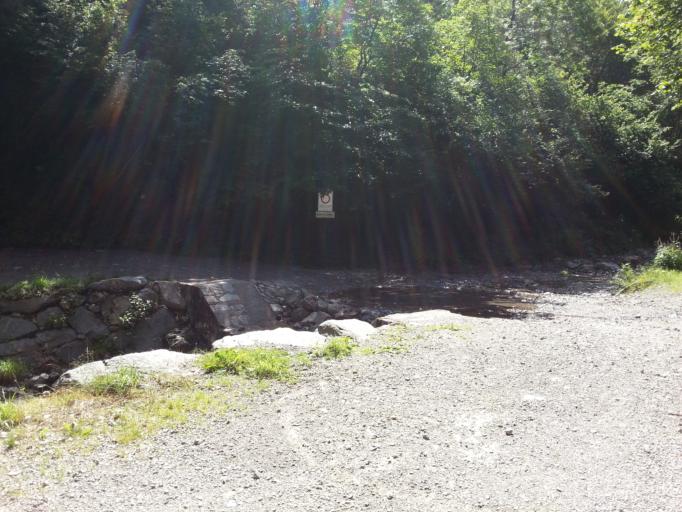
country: IT
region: Lombardy
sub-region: Provincia di Lecco
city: Cremeno
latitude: 45.9192
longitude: 9.4597
